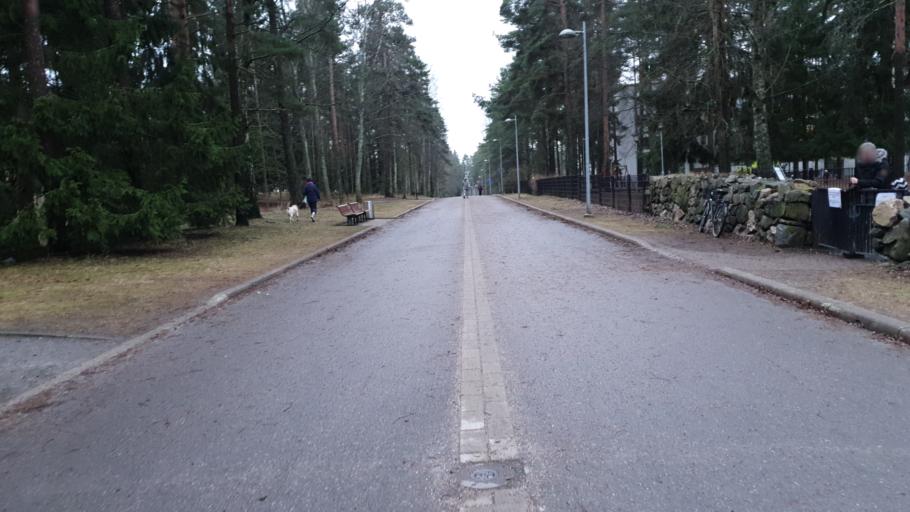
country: FI
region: Uusimaa
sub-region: Helsinki
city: Vantaa
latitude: 60.2232
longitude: 25.0656
